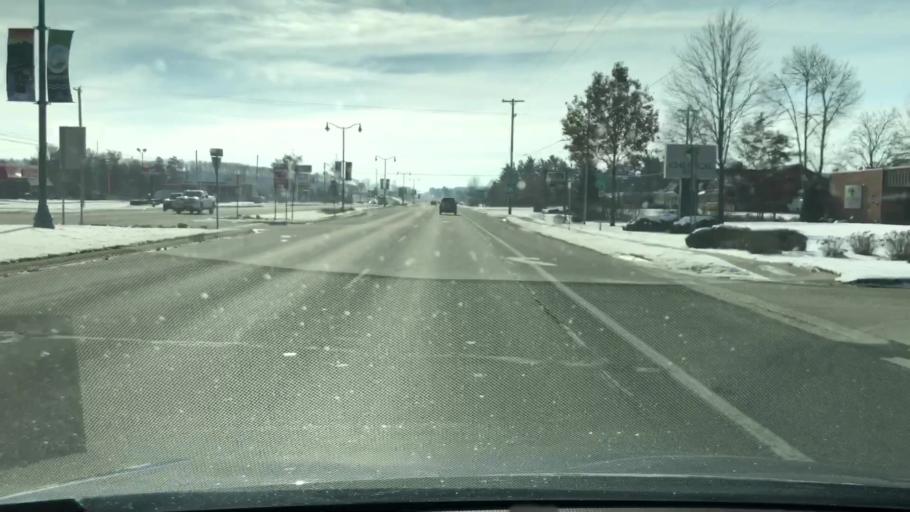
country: US
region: Michigan
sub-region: Crawford County
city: Grayling
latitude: 44.6499
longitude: -84.7086
